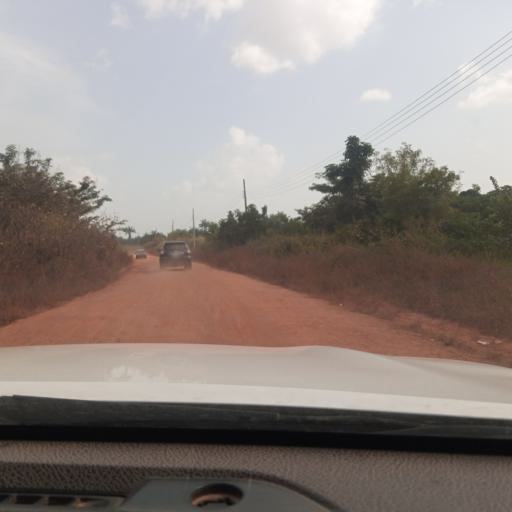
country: NG
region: Osun
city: Ede
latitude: 7.6711
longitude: 4.4690
